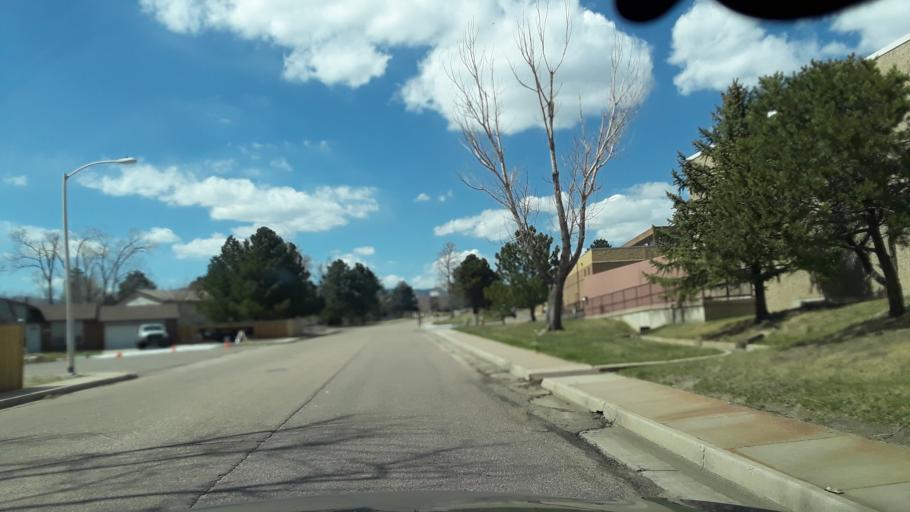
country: US
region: Colorado
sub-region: El Paso County
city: Colorado Springs
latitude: 38.9045
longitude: -104.7812
